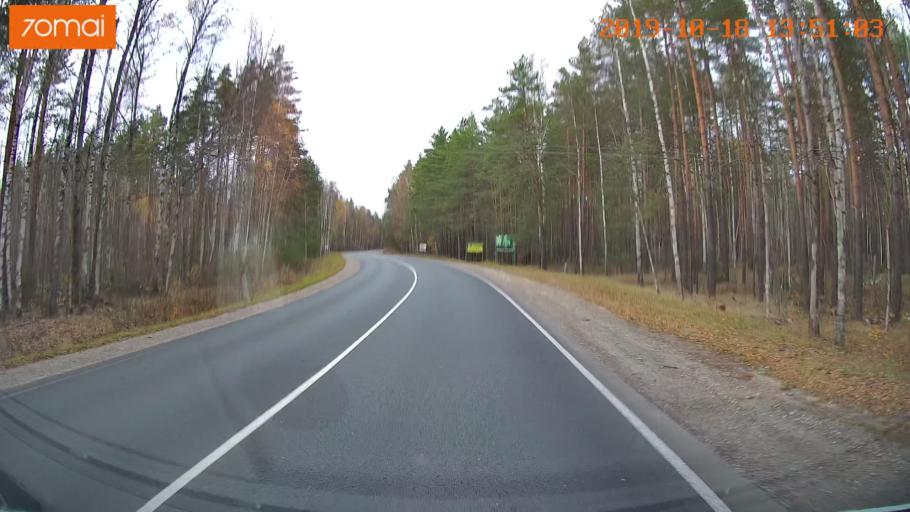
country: RU
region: Moskovskaya
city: Radovitskiy
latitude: 55.0129
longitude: 39.9642
